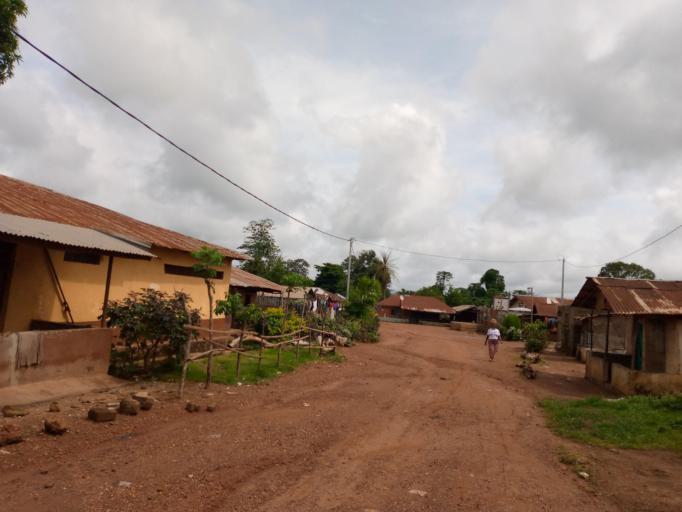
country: SL
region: Southern Province
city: Mogbwemo
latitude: 7.7629
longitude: -12.3085
